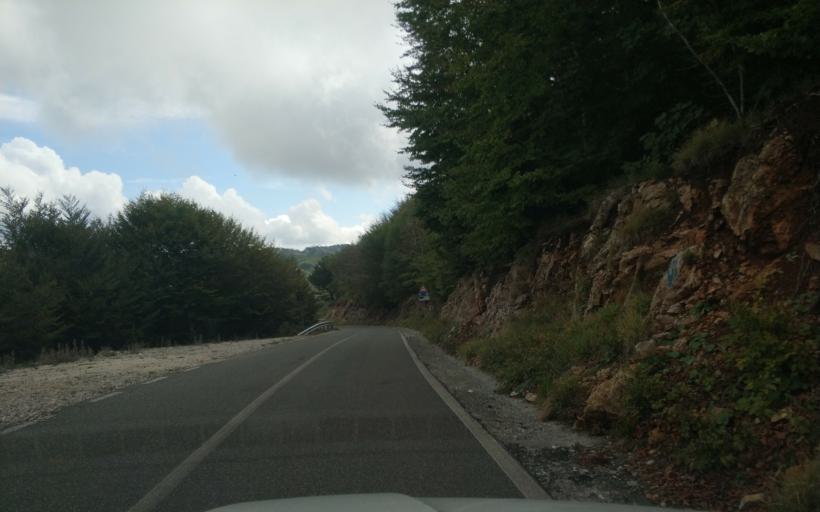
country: AL
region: Durres
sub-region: Rrethi i Krujes
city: Kruje
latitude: 41.5190
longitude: 19.8040
